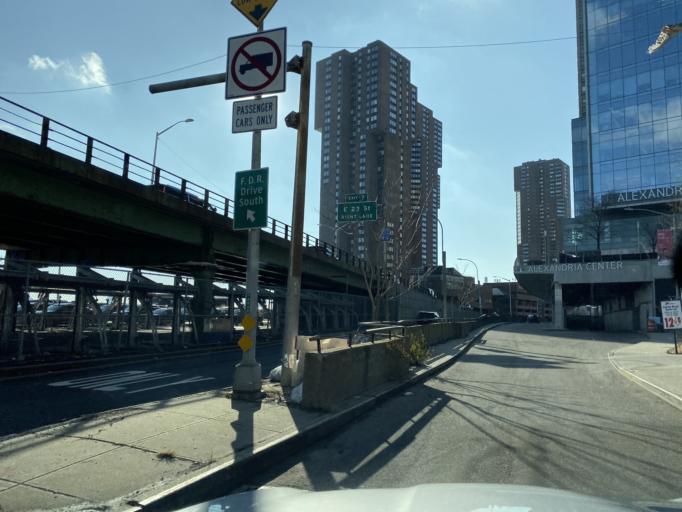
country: US
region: New York
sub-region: Queens County
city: Long Island City
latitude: 40.7403
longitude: -73.9733
